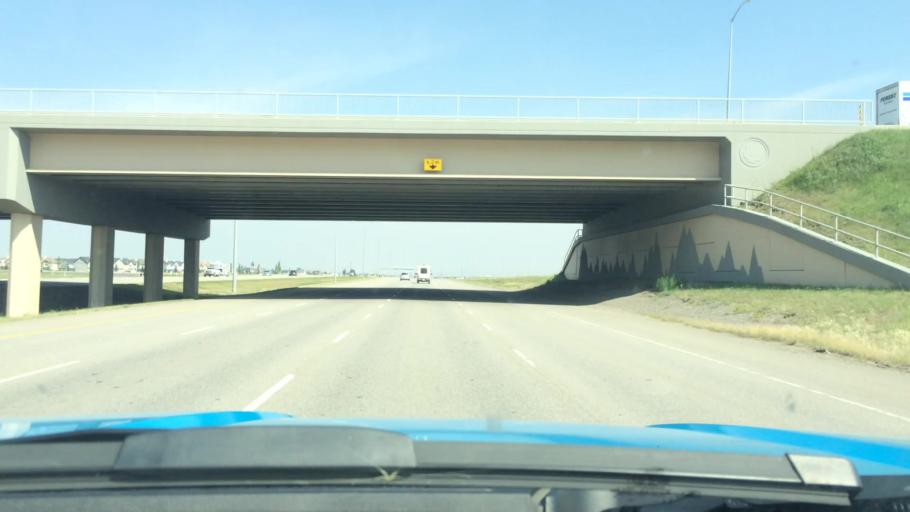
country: CA
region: Alberta
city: Okotoks
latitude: 50.9047
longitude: -113.9481
